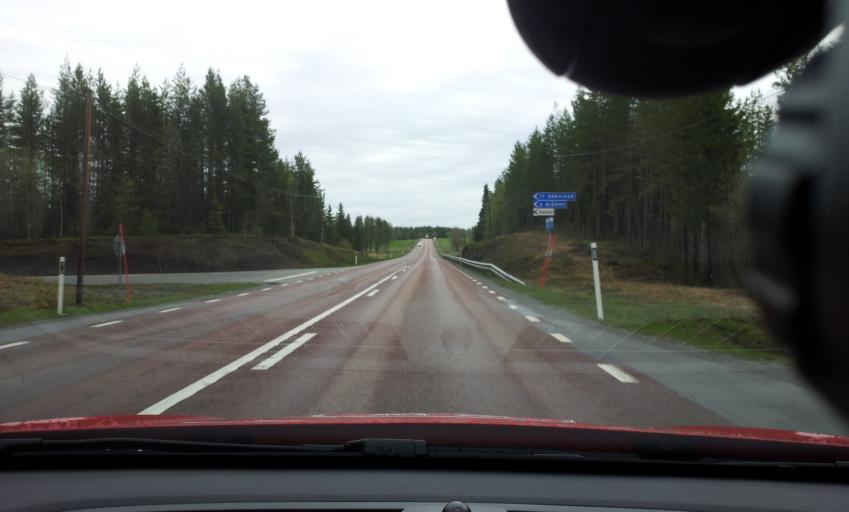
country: SE
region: Jaemtland
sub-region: OEstersunds Kommun
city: Ostersund
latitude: 63.0006
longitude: 14.6412
